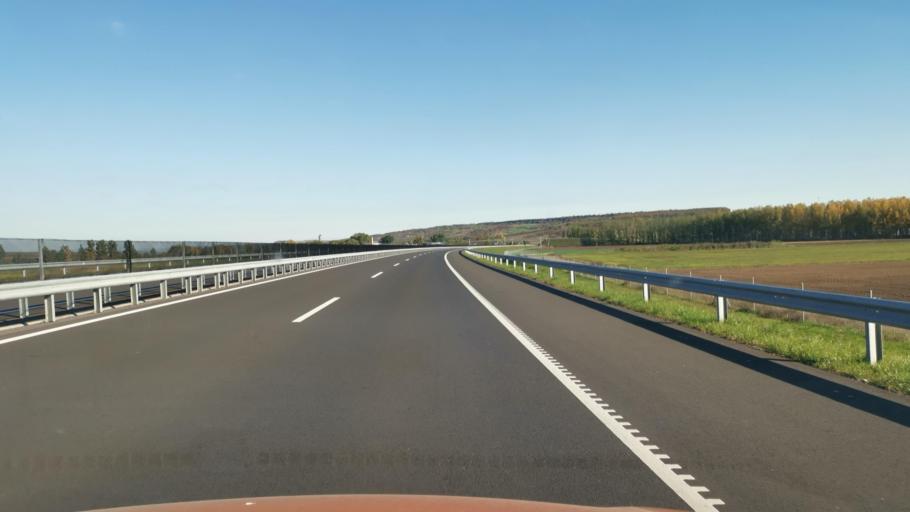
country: HU
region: Borsod-Abauj-Zemplen
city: Szikszo
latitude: 48.2016
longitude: 20.9086
